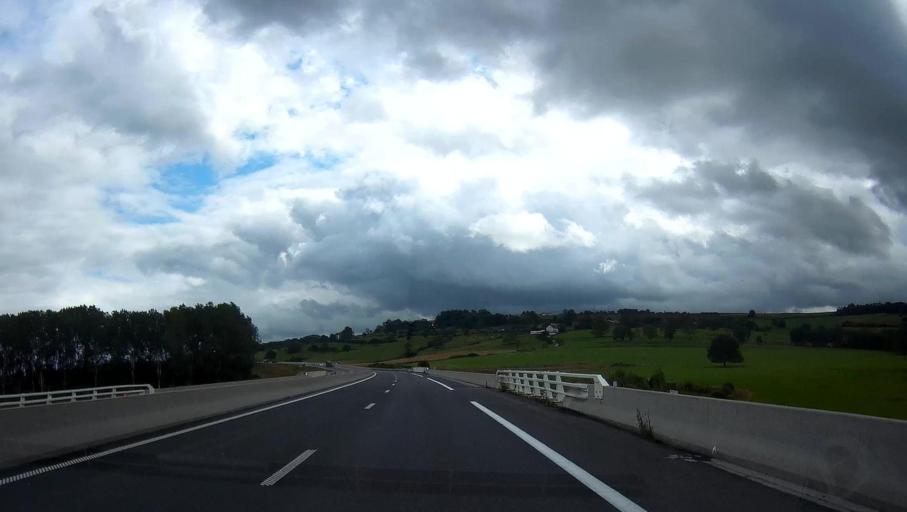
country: FR
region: Champagne-Ardenne
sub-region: Departement des Ardennes
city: Rimogne
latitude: 49.7954
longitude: 4.5381
